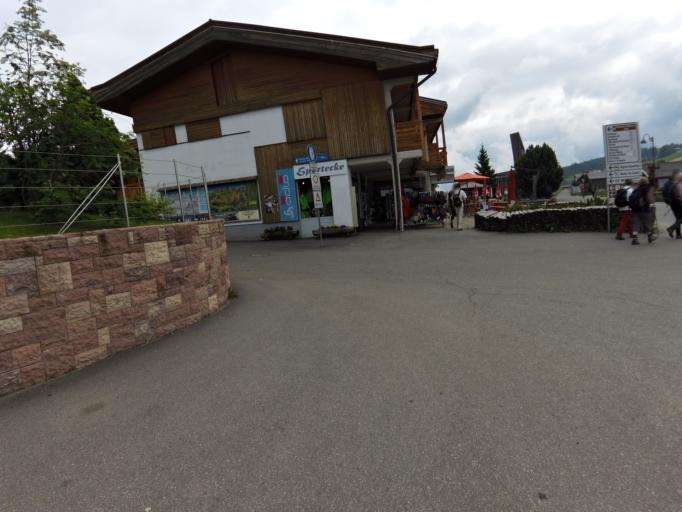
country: IT
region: Trentino-Alto Adige
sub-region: Bolzano
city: Siusi
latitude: 46.5402
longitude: 11.6179
